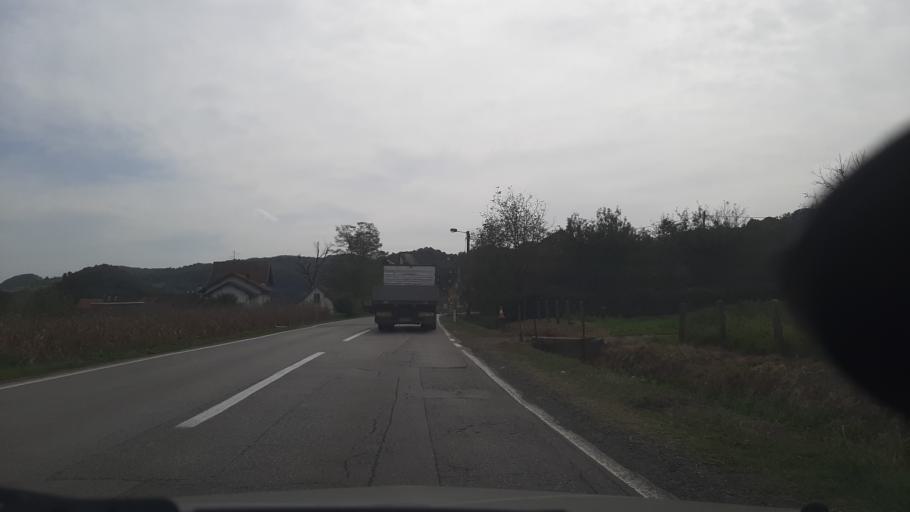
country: BA
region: Republika Srpska
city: Maglajani
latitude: 44.8602
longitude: 17.4378
